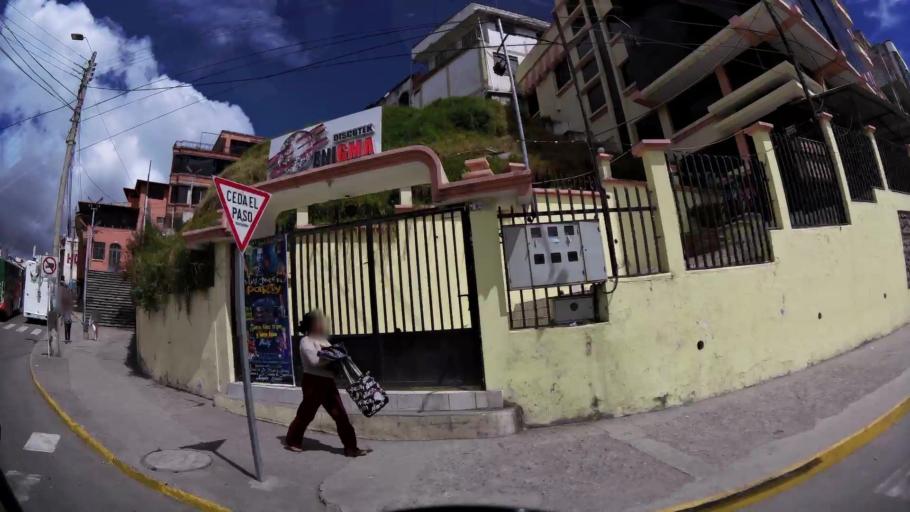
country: EC
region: Canar
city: Azogues
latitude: -2.7373
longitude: -78.8491
